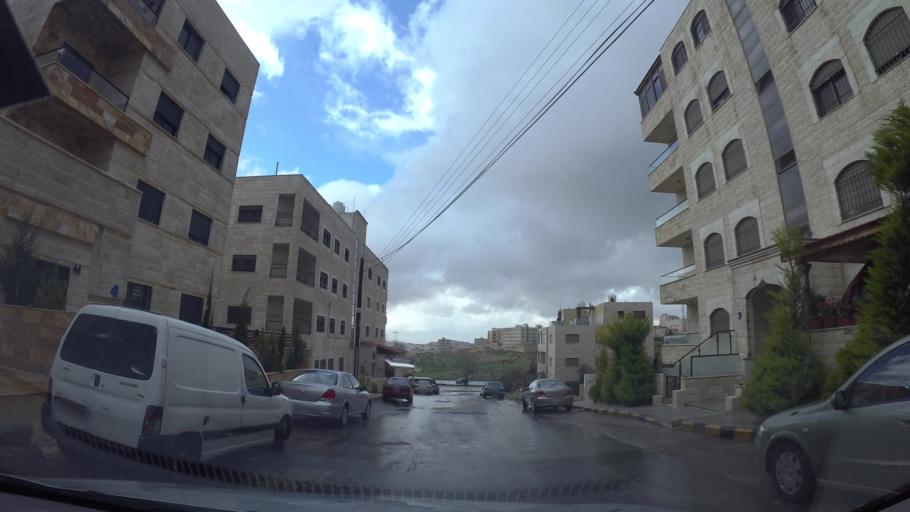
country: JO
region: Amman
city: Al Jubayhah
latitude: 32.0350
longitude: 35.8926
